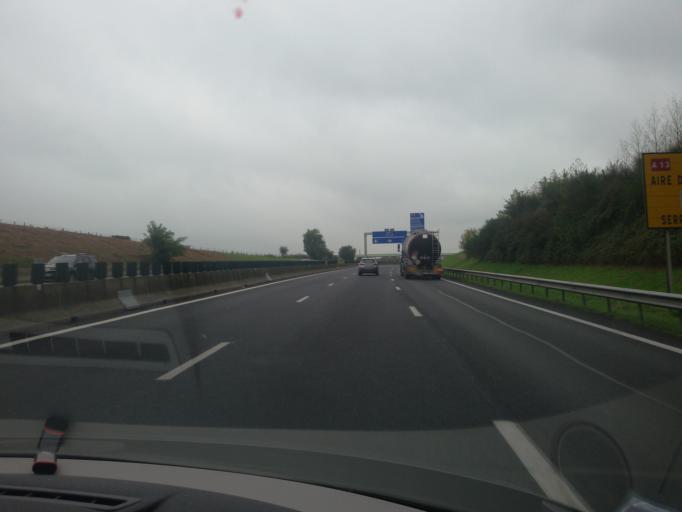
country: FR
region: Haute-Normandie
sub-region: Departement de l'Eure
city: Beuzeville
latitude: 49.3148
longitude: 0.3071
